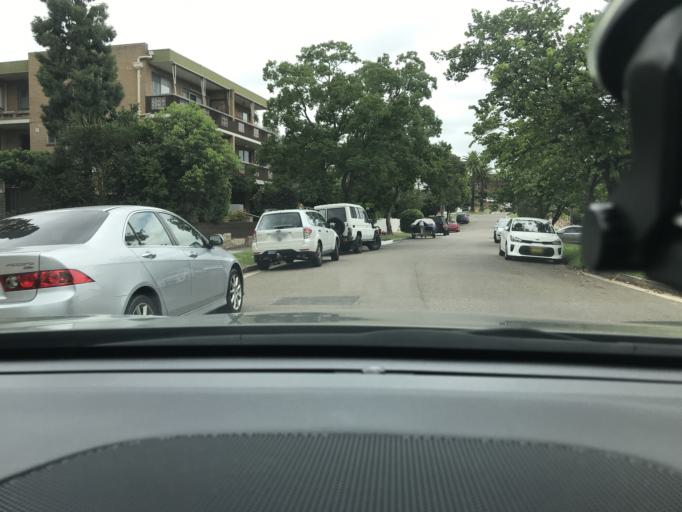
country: AU
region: New South Wales
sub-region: Canada Bay
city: Wareemba
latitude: -33.8512
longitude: 151.1270
